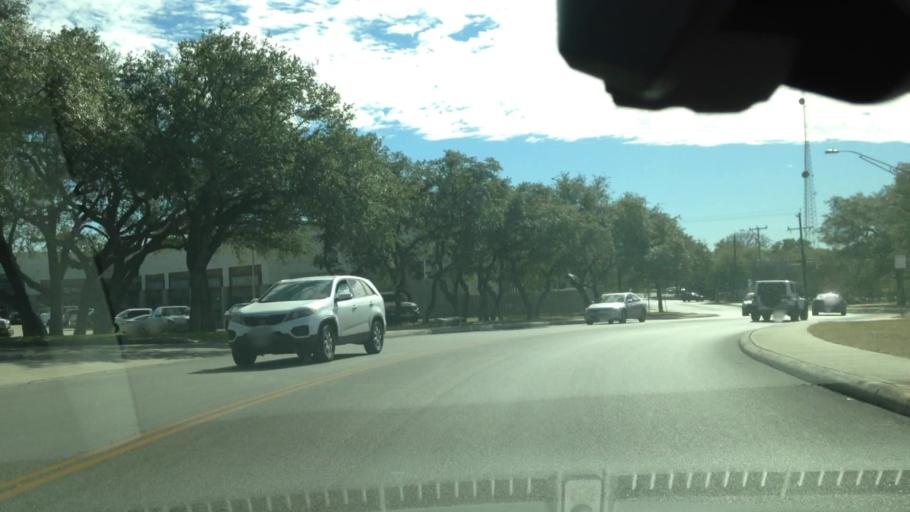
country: US
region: Texas
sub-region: Bexar County
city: Shavano Park
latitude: 29.5523
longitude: -98.5901
